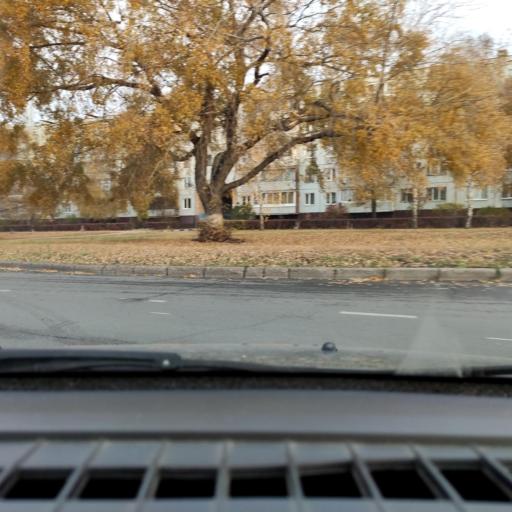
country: RU
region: Samara
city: Tol'yatti
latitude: 53.5285
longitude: 49.2876
